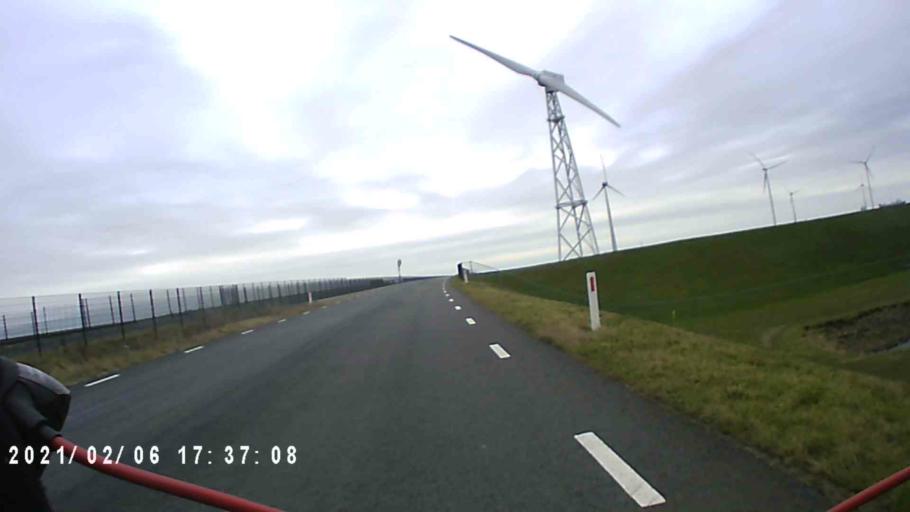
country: NL
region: Groningen
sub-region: Gemeente Appingedam
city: Appingedam
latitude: 53.4531
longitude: 6.7976
